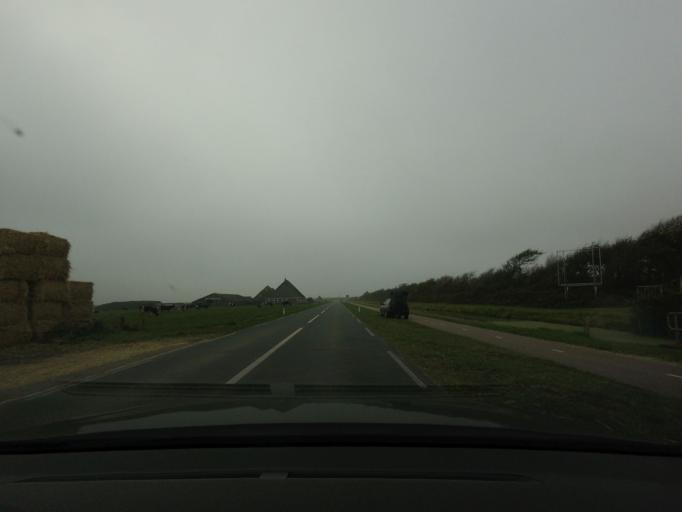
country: NL
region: North Holland
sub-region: Gemeente Schagen
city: Harenkarspel
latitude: 52.7583
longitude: 4.6670
